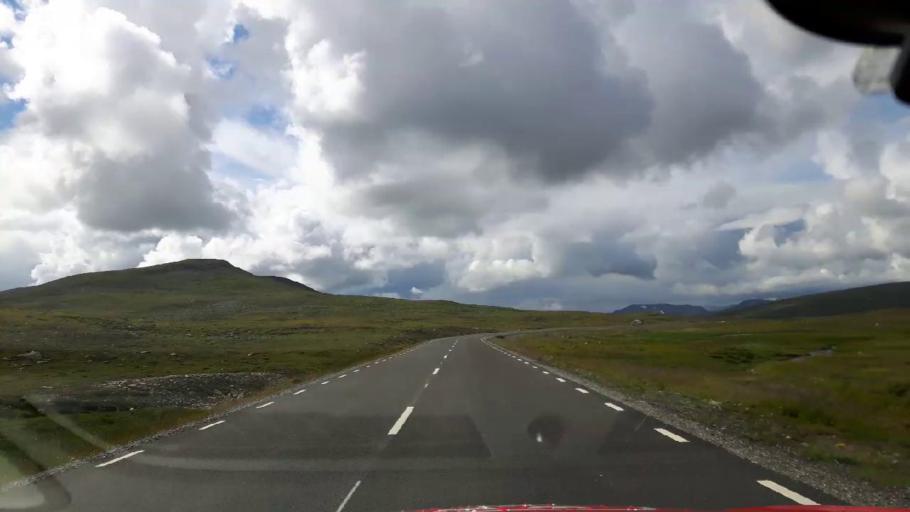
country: NO
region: Nordland
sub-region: Hattfjelldal
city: Hattfjelldal
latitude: 65.0600
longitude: 14.3737
